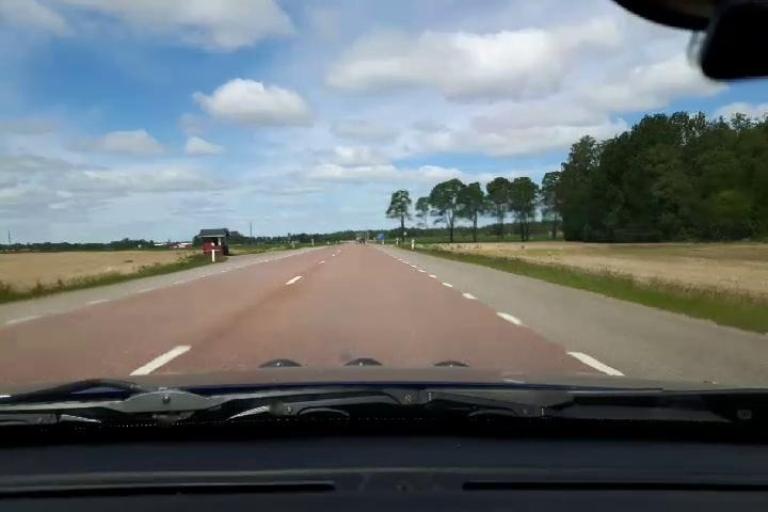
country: SE
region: Uppsala
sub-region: Osthammars Kommun
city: Bjorklinge
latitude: 60.0120
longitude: 17.5594
